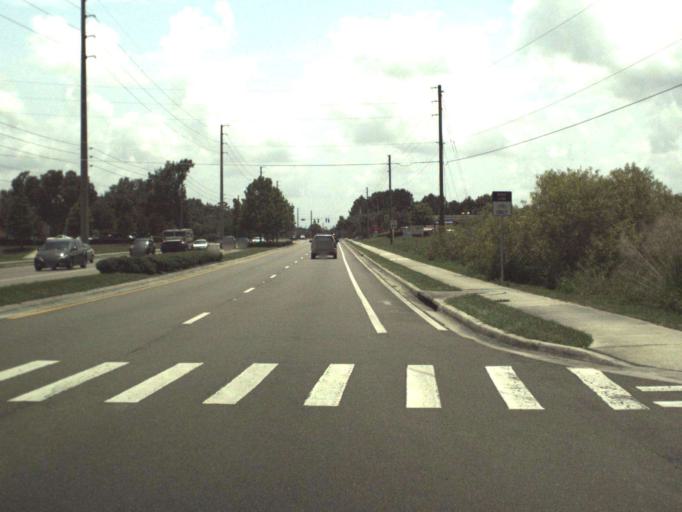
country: US
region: Florida
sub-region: Seminole County
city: Goldenrod
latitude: 28.6262
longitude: -81.2450
